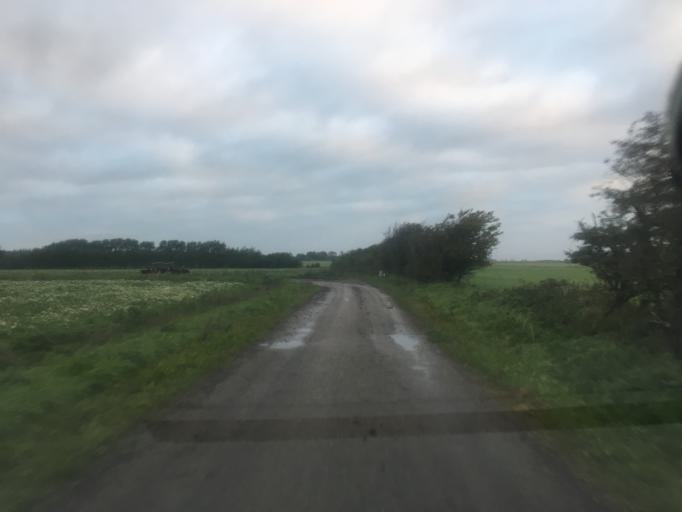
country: DK
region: South Denmark
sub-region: Tonder Kommune
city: Logumkloster
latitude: 54.9882
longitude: 8.9321
